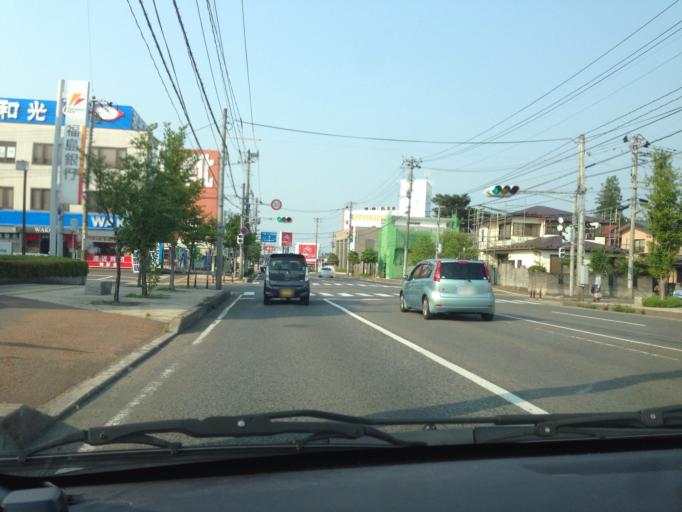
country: JP
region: Tochigi
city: Kuroiso
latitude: 37.1242
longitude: 140.1959
